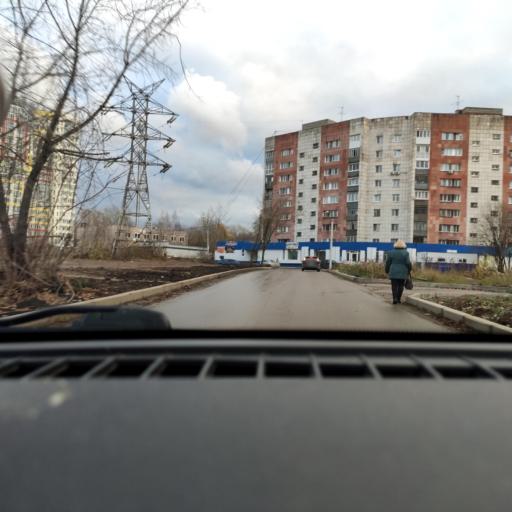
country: RU
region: Perm
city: Perm
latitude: 57.9721
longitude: 56.2704
